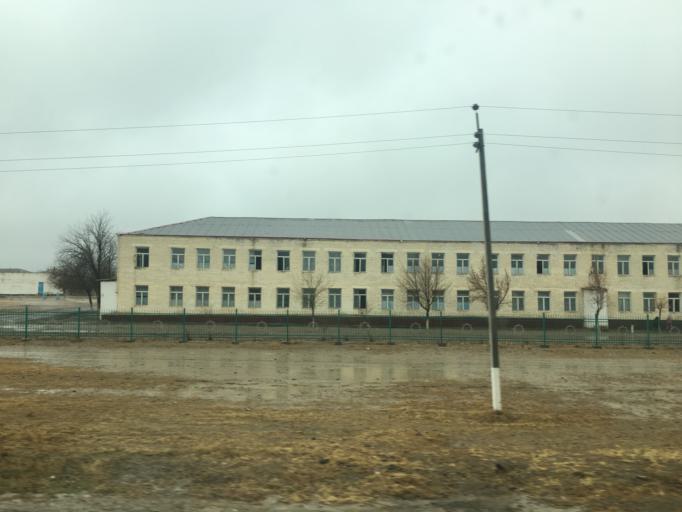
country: TM
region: Mary
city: Yoloeten
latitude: 37.3271
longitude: 62.3012
